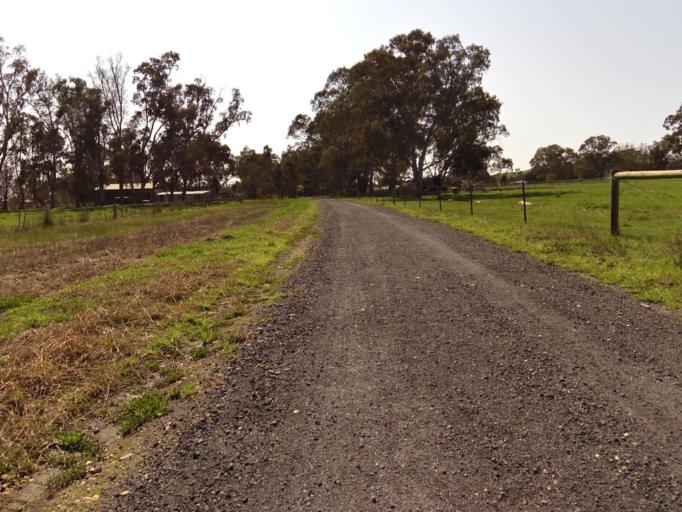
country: AU
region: Victoria
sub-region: Murrindindi
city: Alexandra
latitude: -37.1099
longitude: 145.6123
